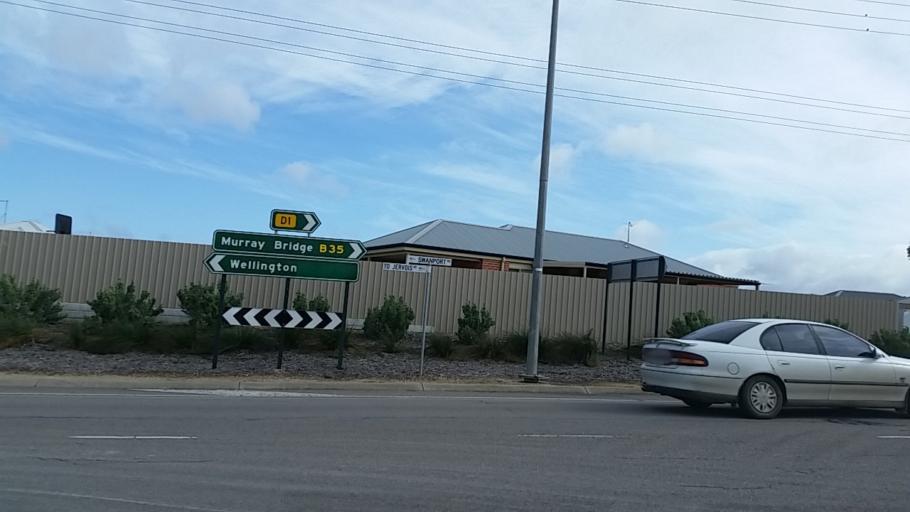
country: AU
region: South Australia
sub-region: Murray Bridge
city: Murray Bridge
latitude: -35.1489
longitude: 139.2863
